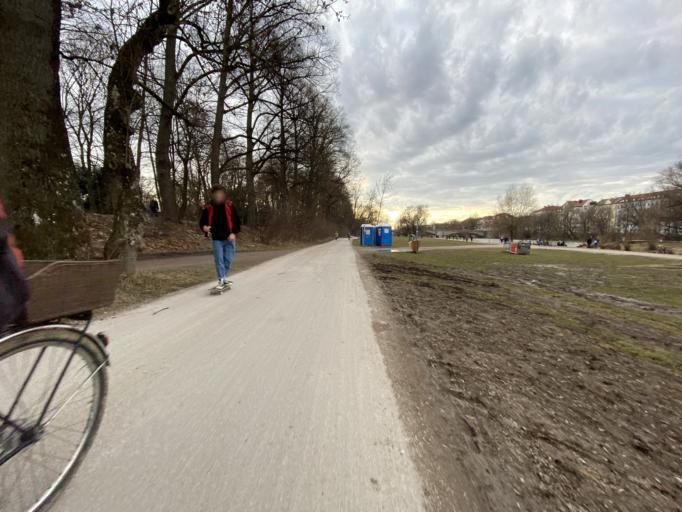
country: DE
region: Bavaria
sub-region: Upper Bavaria
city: Munich
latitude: 48.1239
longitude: 11.5721
